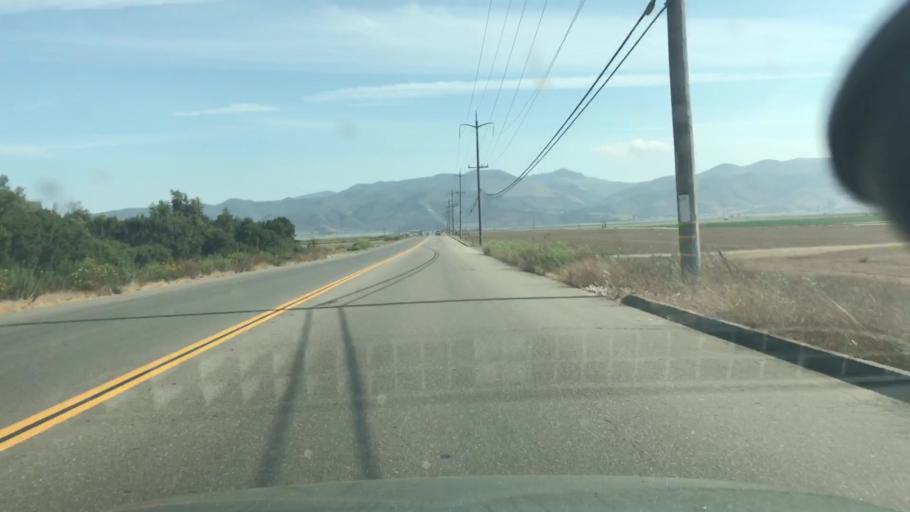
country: US
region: California
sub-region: Santa Barbara County
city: Vandenberg Village
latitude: 34.6702
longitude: -120.4928
